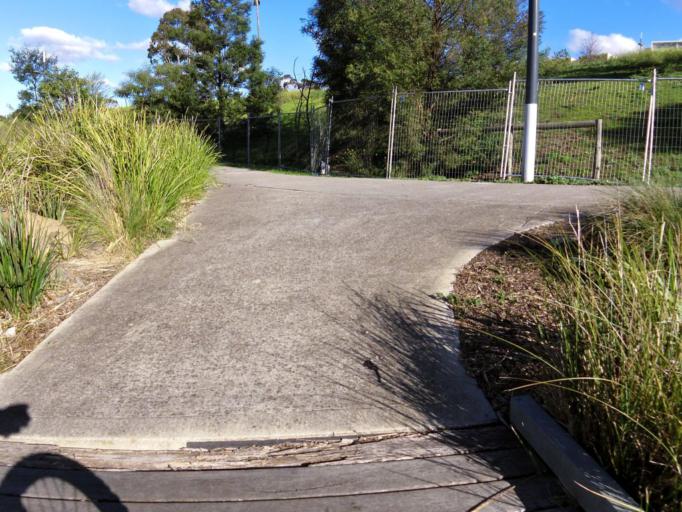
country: AU
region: Victoria
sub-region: Whittlesea
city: Mill Park
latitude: -37.6820
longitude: 145.0761
